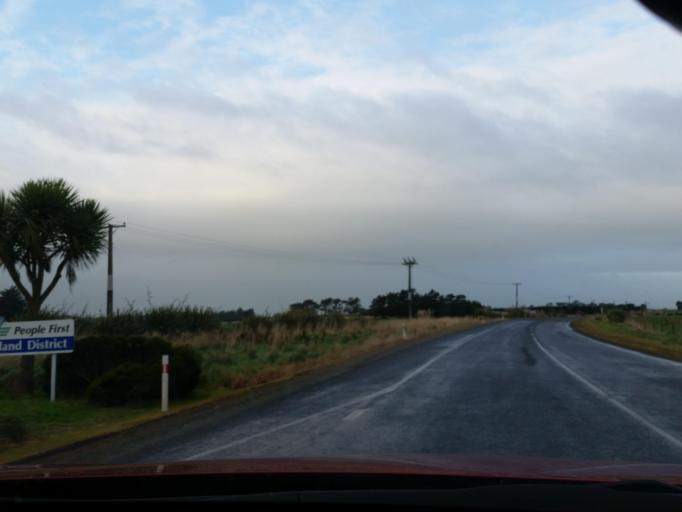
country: NZ
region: Southland
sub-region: Invercargill City
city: Invercargill
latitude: -46.4512
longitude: 168.4586
